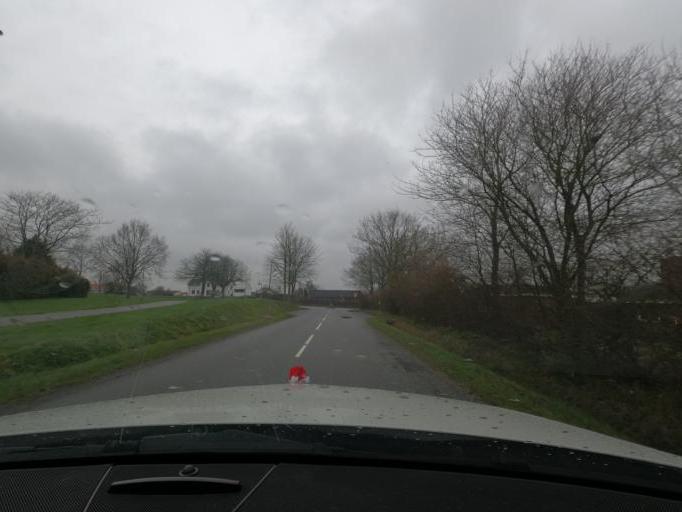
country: DK
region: South Denmark
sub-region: Haderslev Kommune
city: Starup
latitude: 55.2354
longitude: 9.5458
